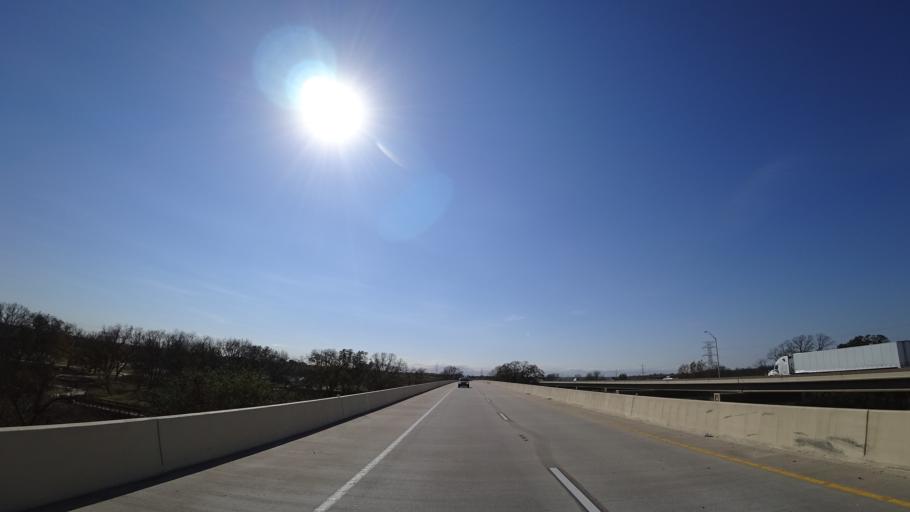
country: US
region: Texas
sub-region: Travis County
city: Garfield
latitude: 30.1886
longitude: -97.6267
